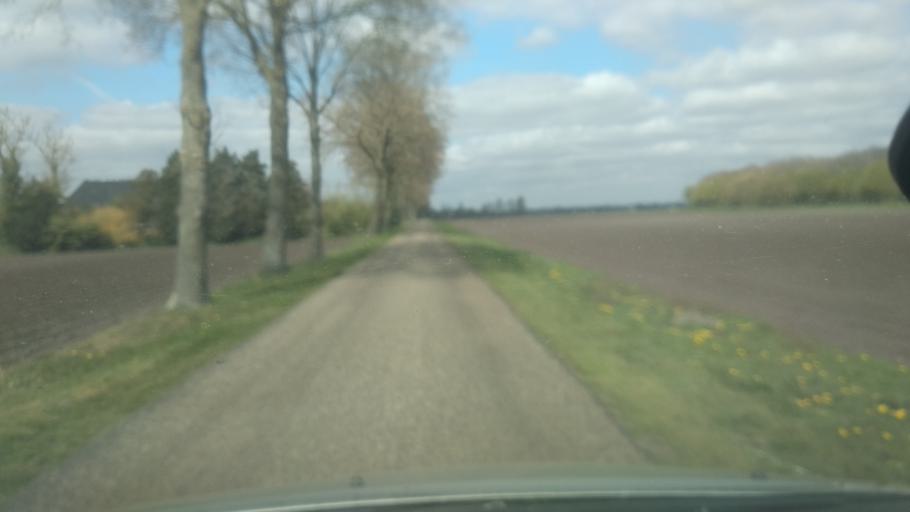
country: NL
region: Drenthe
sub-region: Gemeente Emmen
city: Emmer-Compascuum
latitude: 52.8878
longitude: 7.0239
